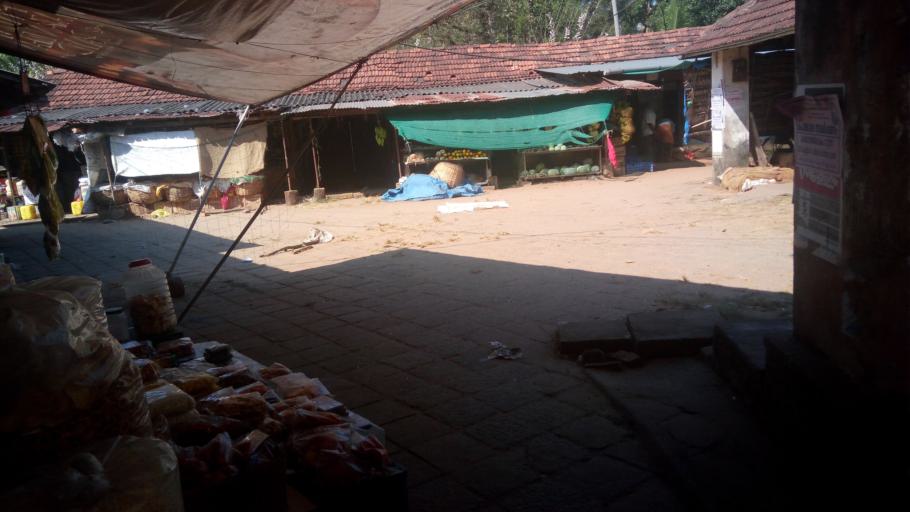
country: IN
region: Kerala
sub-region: Alappuzha
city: Shertallai
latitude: 9.6422
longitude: 76.3703
